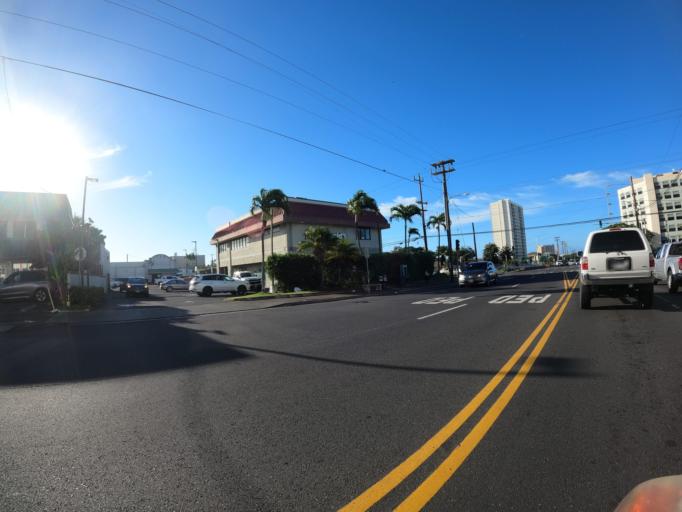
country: US
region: Hawaii
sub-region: Honolulu County
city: Honolulu
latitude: 21.3219
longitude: -157.8597
